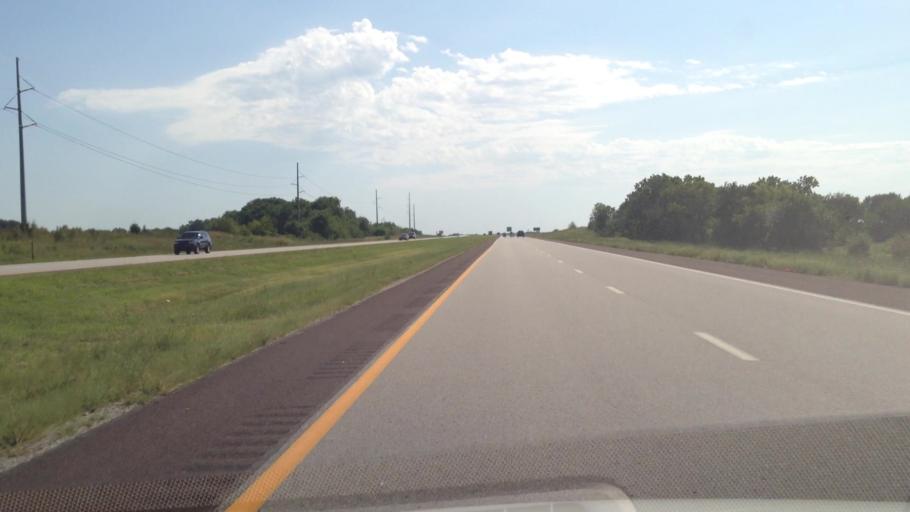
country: US
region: Kansas
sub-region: Miami County
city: Louisburg
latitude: 38.6442
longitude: -94.6899
